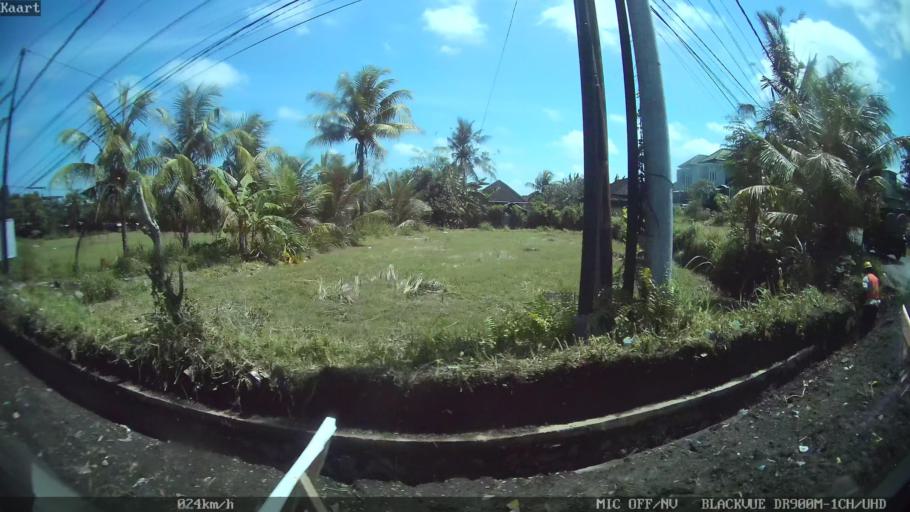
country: ID
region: Bali
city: Banjar Kelodan
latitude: -8.5363
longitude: 115.3348
